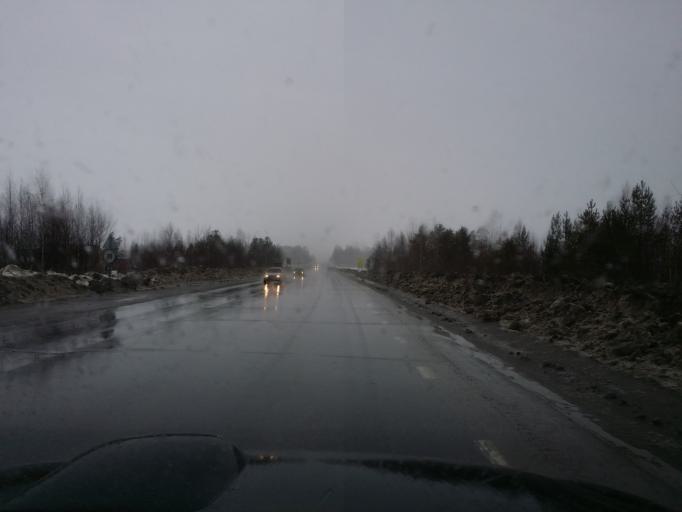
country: RU
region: Khanty-Mansiyskiy Avtonomnyy Okrug
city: Izluchinsk
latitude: 60.9647
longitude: 76.7697
